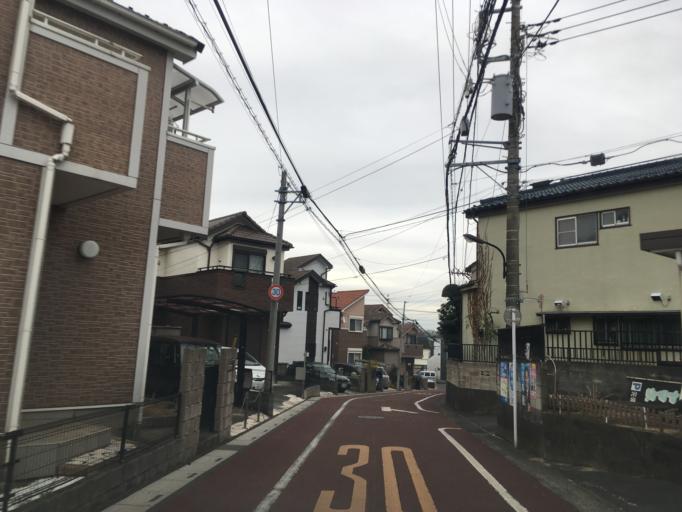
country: JP
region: Tokyo
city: Higashimurayama-shi
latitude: 35.7512
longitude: 139.4848
